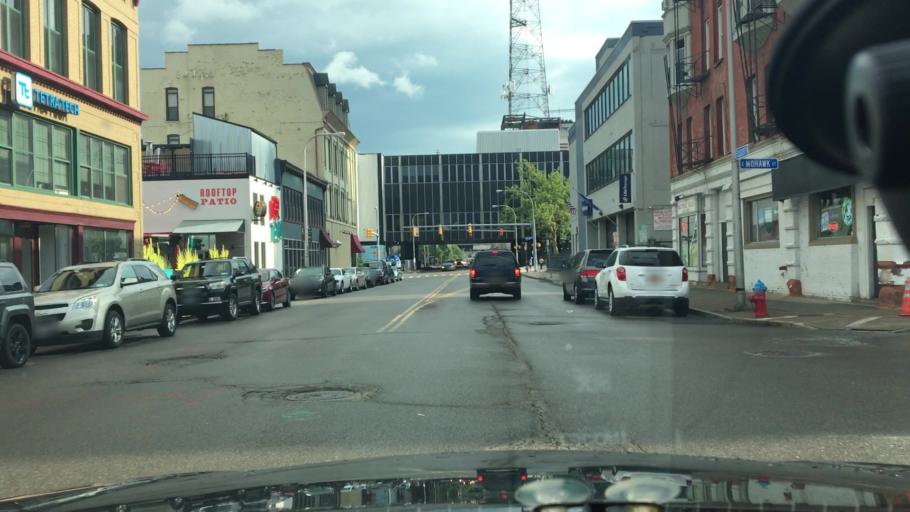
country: US
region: New York
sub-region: Erie County
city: Buffalo
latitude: 42.8868
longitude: -78.8717
